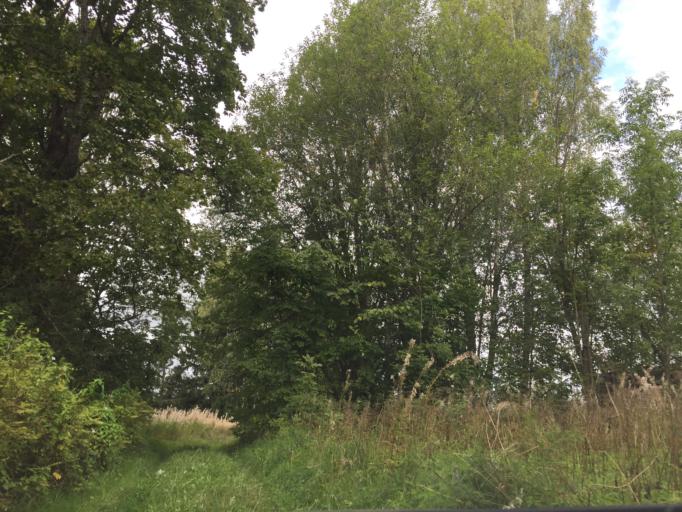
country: LV
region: Pargaujas
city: Stalbe
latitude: 57.4909
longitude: 24.9126
